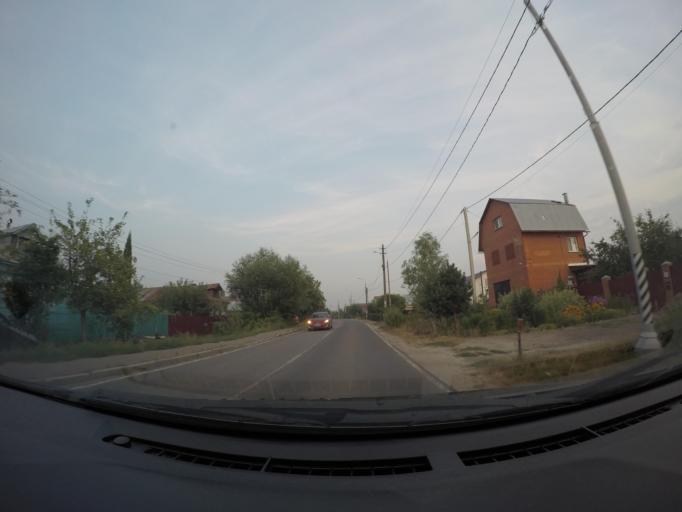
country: RU
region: Moskovskaya
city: Imeni Tsyurupy
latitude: 55.4929
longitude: 38.6659
